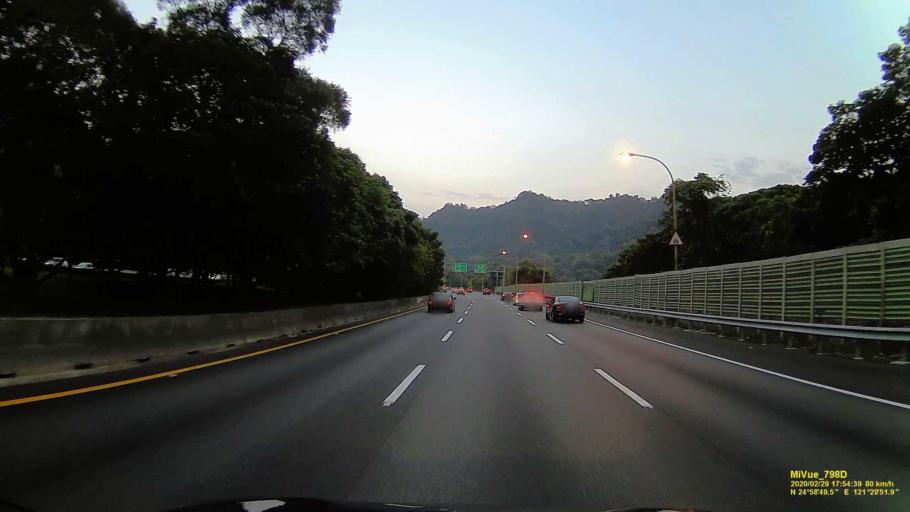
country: TW
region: Taipei
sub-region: Taipei
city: Banqiao
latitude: 24.9802
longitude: 121.4980
